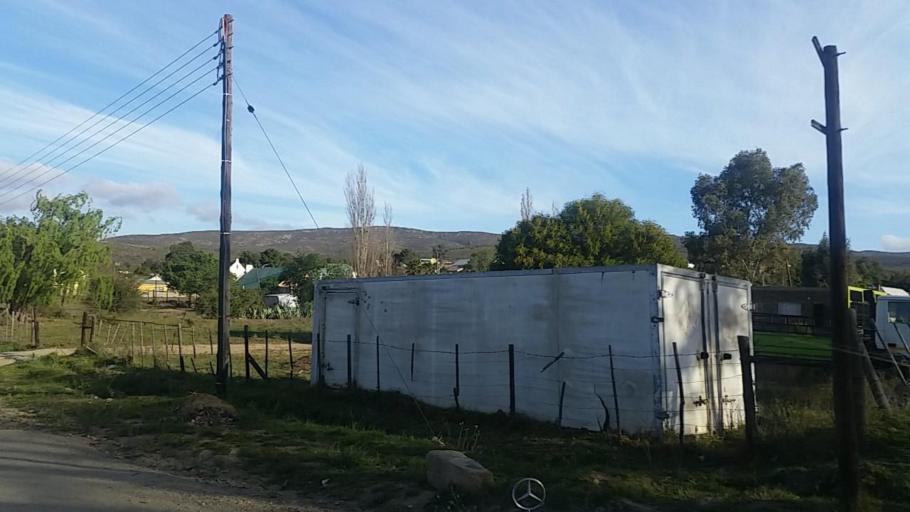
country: ZA
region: Western Cape
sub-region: Eden District Municipality
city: Knysna
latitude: -33.6572
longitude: 23.1184
